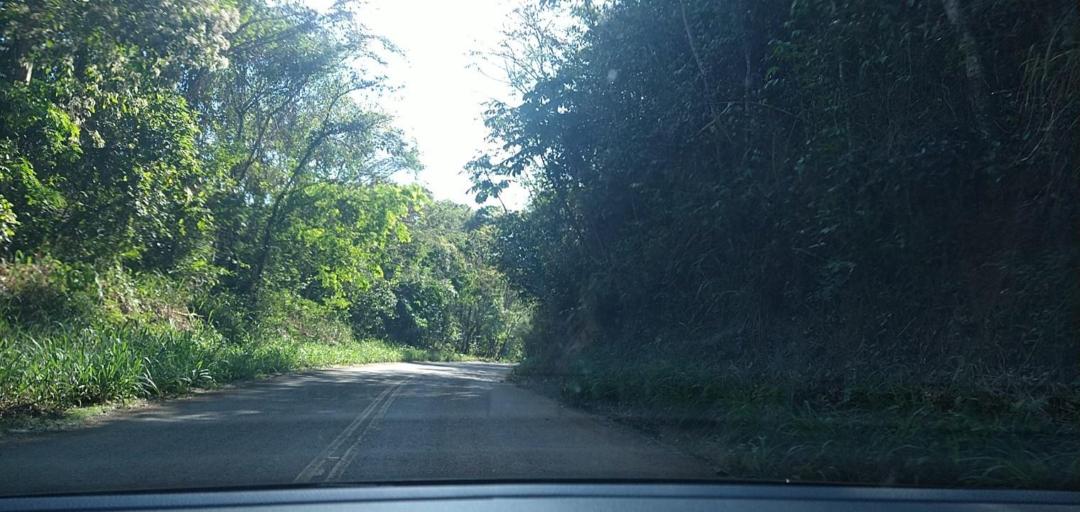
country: BR
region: Minas Gerais
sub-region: Alvinopolis
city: Alvinopolis
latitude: -20.1761
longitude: -42.9282
